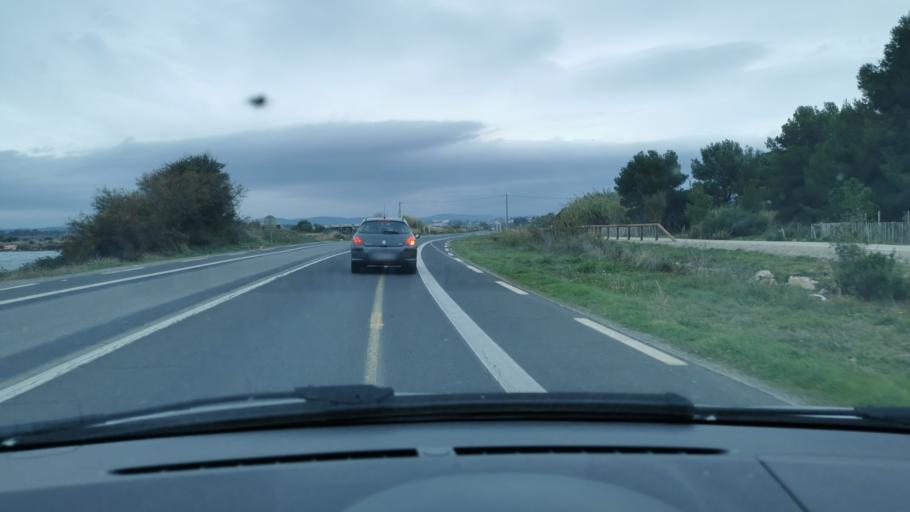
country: FR
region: Languedoc-Roussillon
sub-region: Departement de l'Herault
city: Balaruc-les-Bains
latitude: 43.4322
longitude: 3.7032
